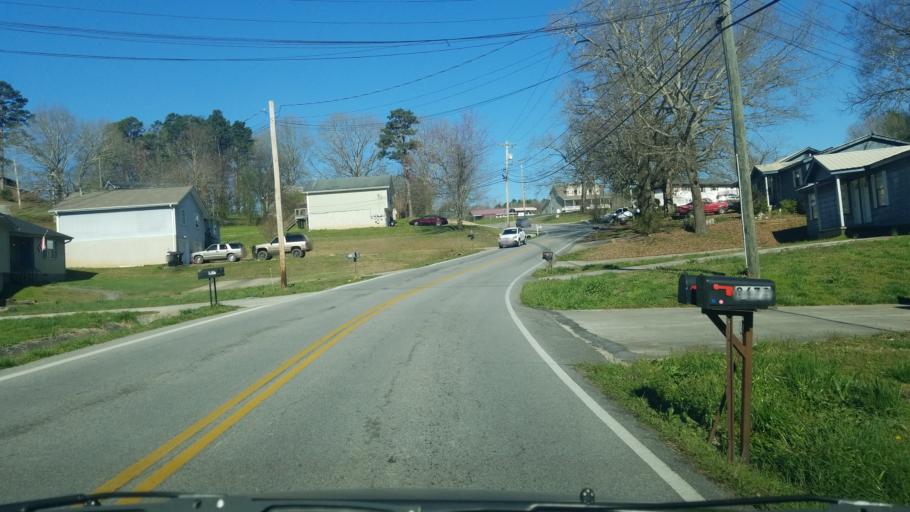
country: US
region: Tennessee
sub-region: Hamilton County
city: Middle Valley
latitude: 35.2141
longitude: -85.1774
